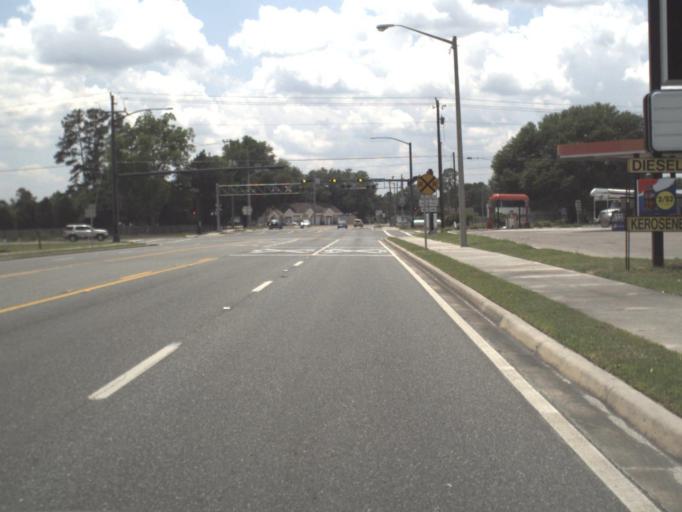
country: US
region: Florida
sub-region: Columbia County
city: Watertown
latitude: 30.1847
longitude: -82.5994
